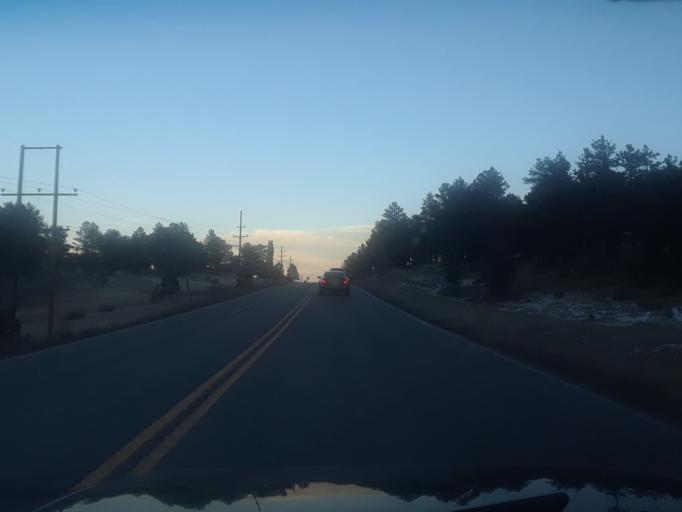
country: US
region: Colorado
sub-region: Clear Creek County
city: Georgetown
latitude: 39.4304
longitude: -105.5750
